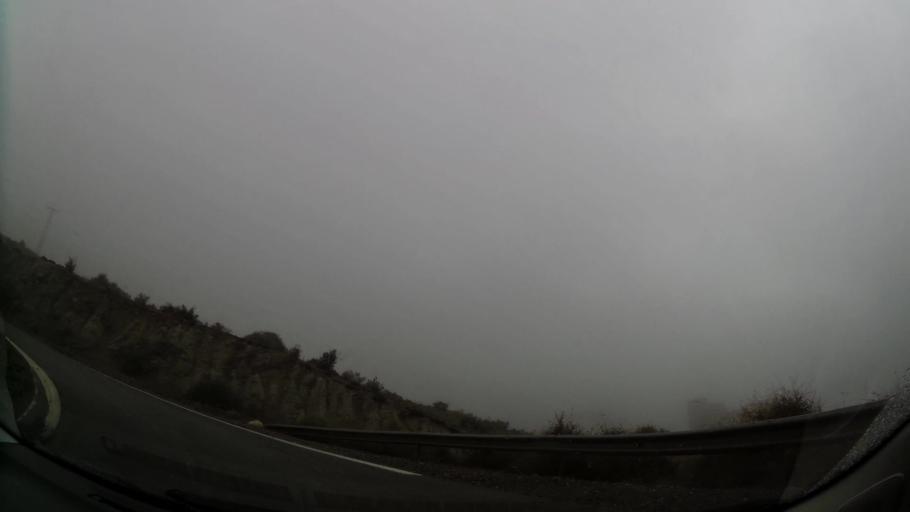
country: MA
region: Taza-Al Hoceima-Taounate
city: Tirhanimine
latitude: 35.2340
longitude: -3.9718
